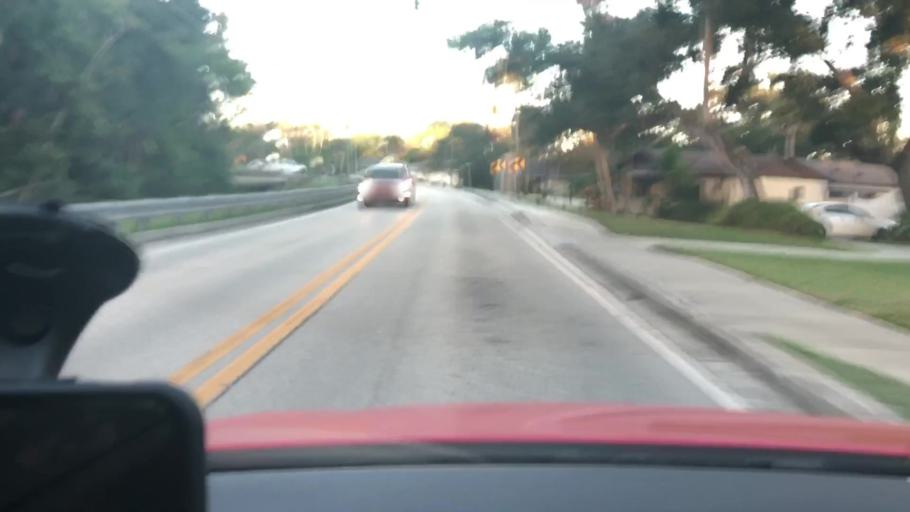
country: US
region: Florida
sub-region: Volusia County
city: South Daytona
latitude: 29.1585
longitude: -81.0092
